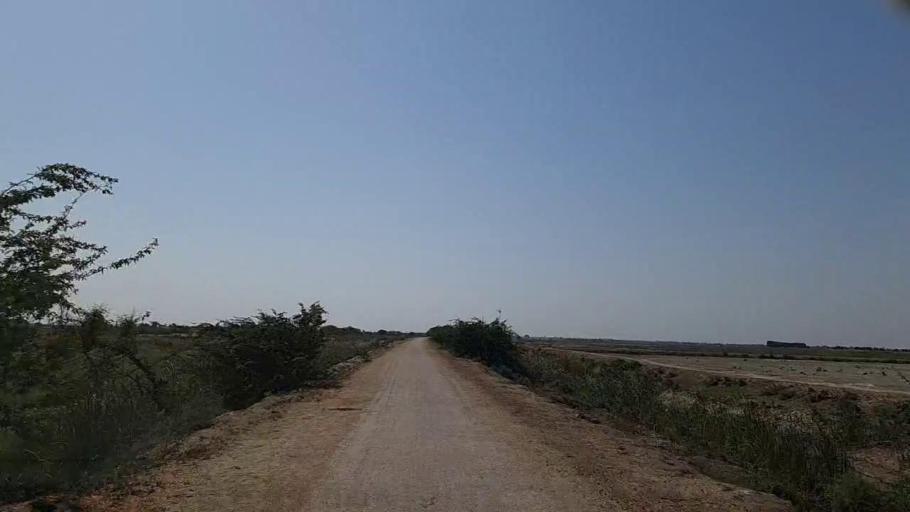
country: PK
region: Sindh
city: Mirpur Batoro
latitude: 24.6761
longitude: 68.3051
